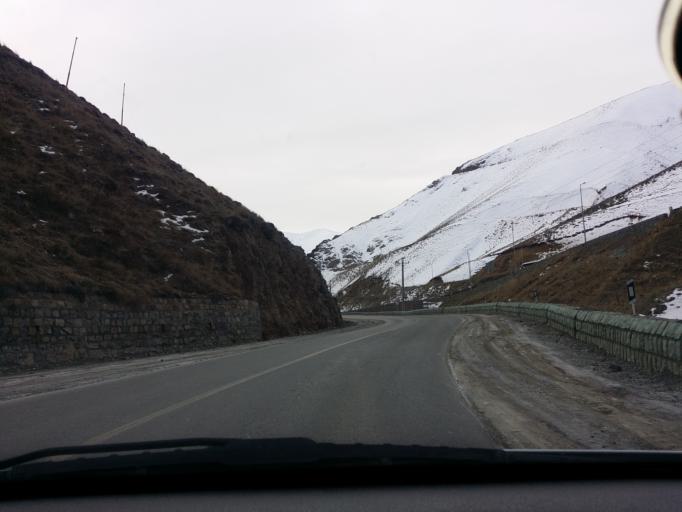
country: IR
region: Tehran
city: Tajrish
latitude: 36.1745
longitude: 51.3151
